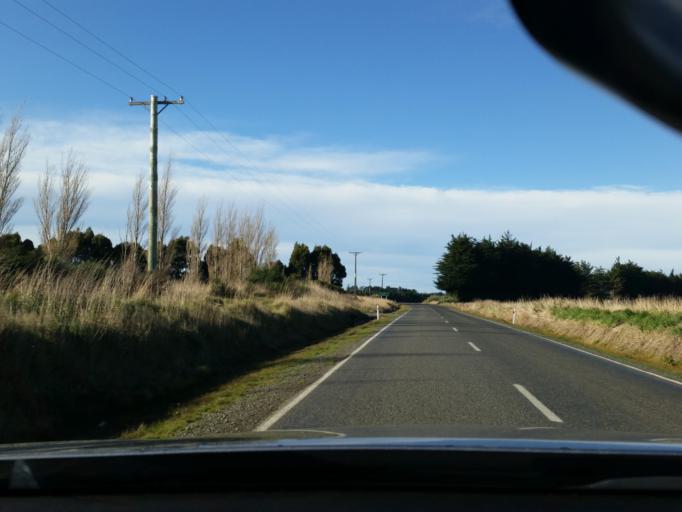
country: NZ
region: Southland
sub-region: Southland District
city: Riverton
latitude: -46.1684
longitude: 168.0869
